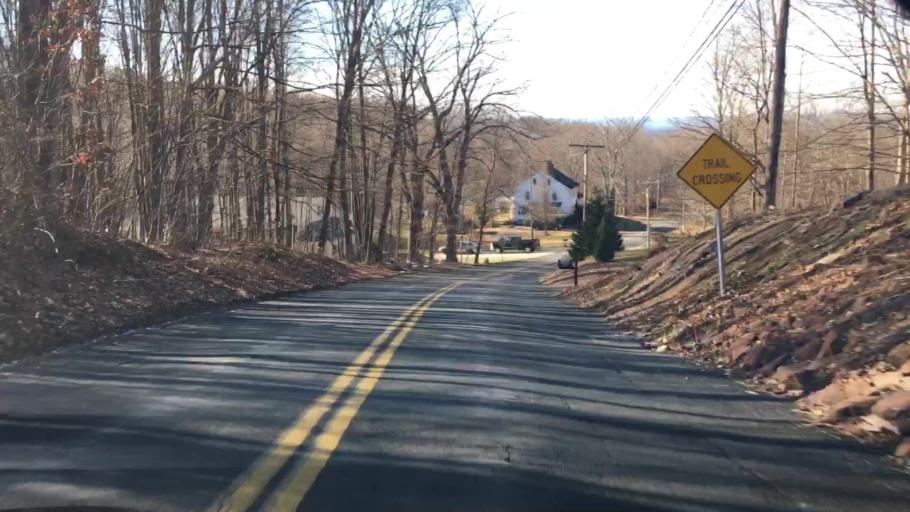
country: US
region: Connecticut
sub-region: Tolland County
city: Somers
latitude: 41.9690
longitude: -72.4303
